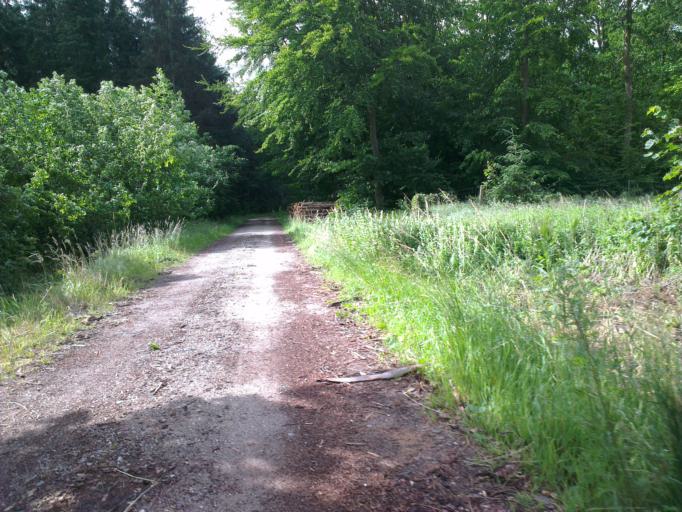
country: DK
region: Capital Region
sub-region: Frederikssund Kommune
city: Jaegerspris
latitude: 55.8833
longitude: 11.9868
